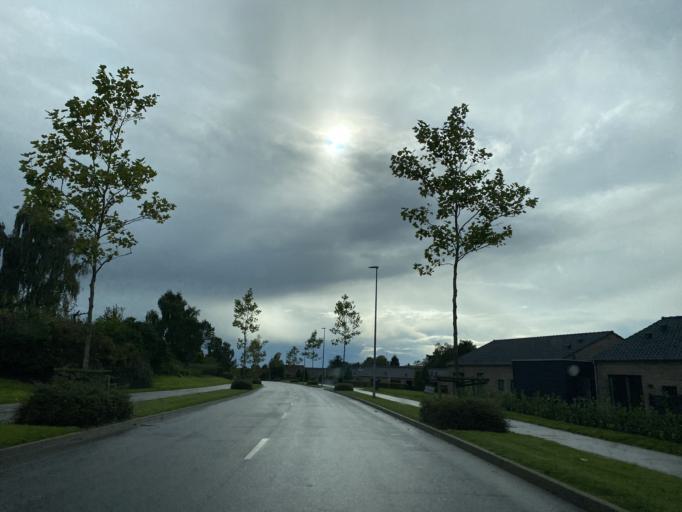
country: DK
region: South Denmark
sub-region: Haderslev Kommune
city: Haderslev
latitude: 55.2593
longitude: 9.4679
